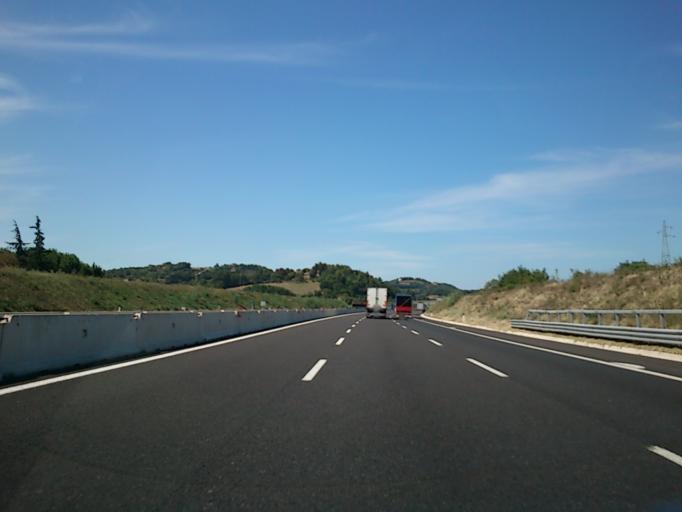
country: IT
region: The Marches
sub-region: Provincia di Pesaro e Urbino
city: Fenile
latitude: 43.8423
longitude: 12.9758
